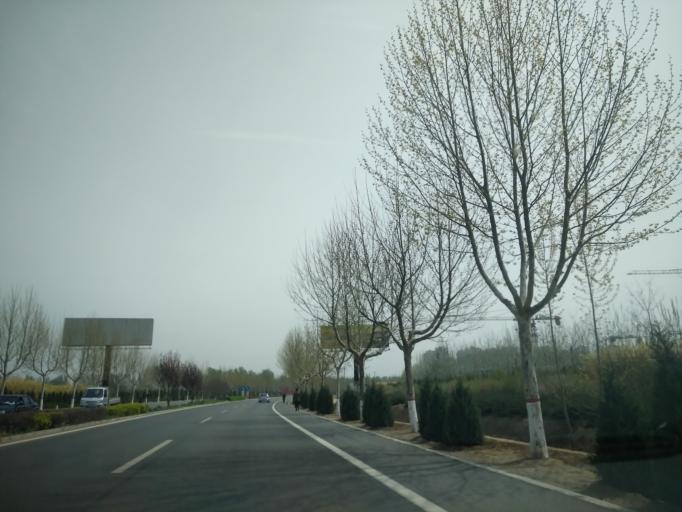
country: CN
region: Beijing
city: Xiji
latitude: 39.7930
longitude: 116.9375
